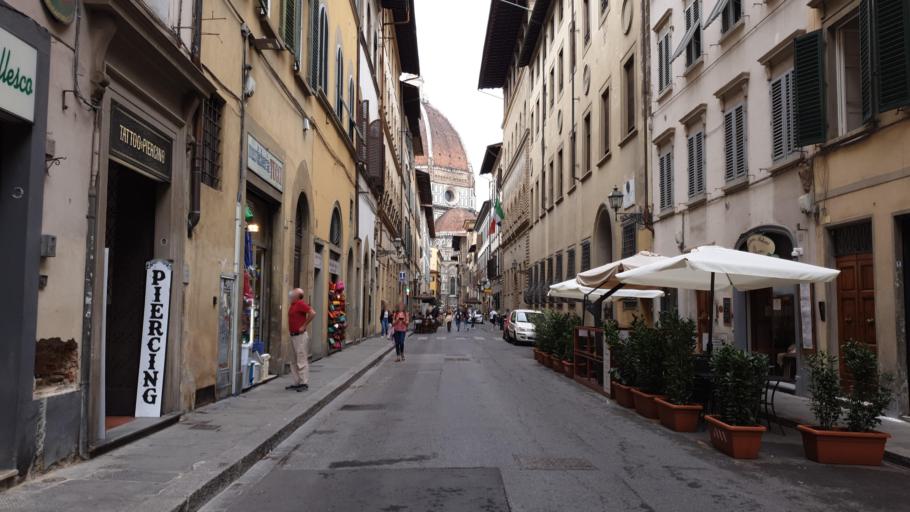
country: IT
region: Tuscany
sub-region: Province of Florence
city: Florence
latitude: 43.7753
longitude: 11.2595
